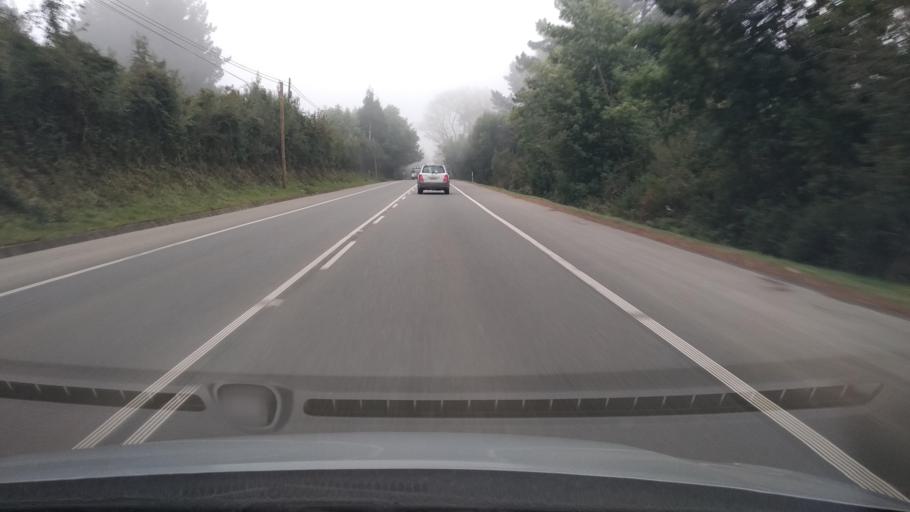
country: CL
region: Los Lagos
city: Las Animas
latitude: -39.7330
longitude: -73.2094
